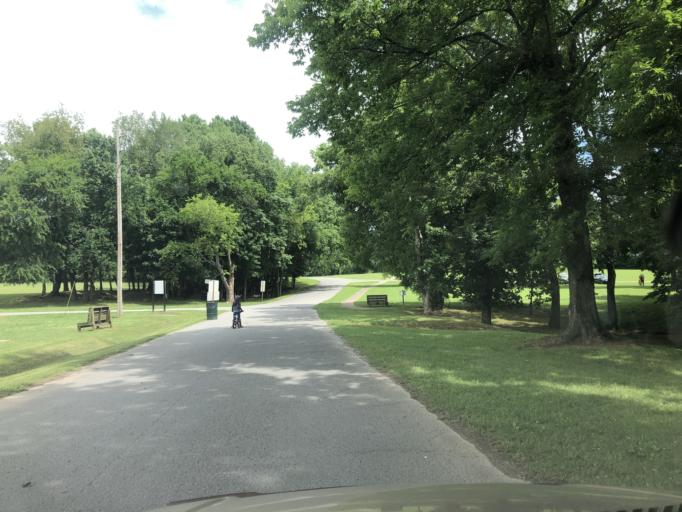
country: US
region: Tennessee
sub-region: Davidson County
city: Lakewood
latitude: 36.2529
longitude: -86.6036
